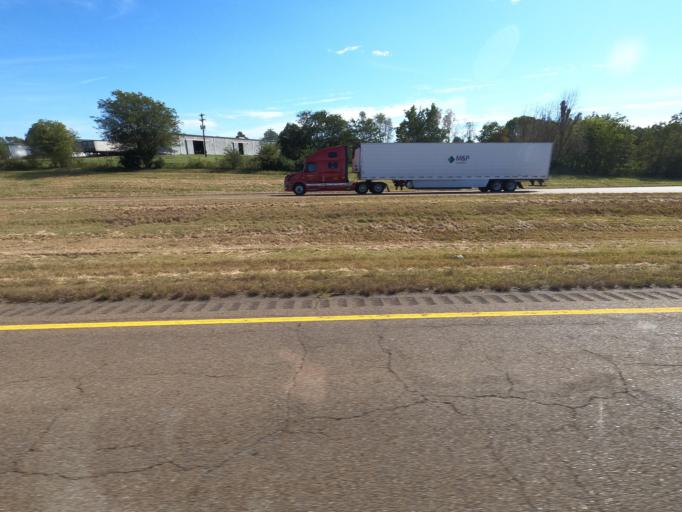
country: US
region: Tennessee
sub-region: Obion County
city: South Fulton
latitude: 36.4941
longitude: -88.9153
